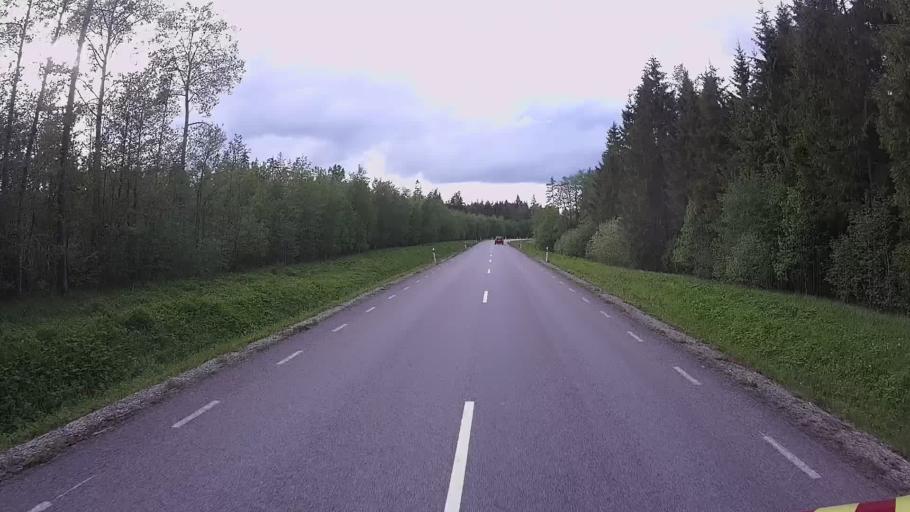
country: EE
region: Jogevamaa
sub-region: Mustvee linn
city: Mustvee
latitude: 59.0603
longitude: 27.0054
